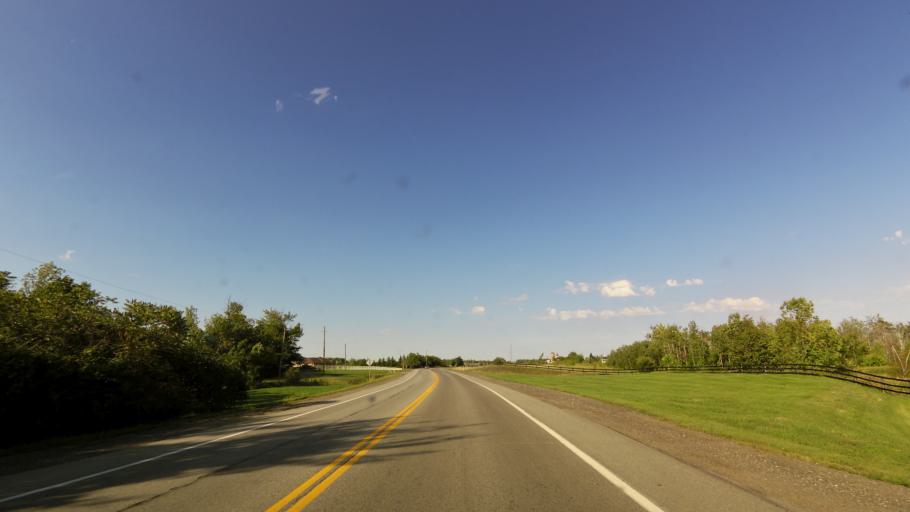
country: CA
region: Ontario
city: Brampton
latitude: 43.7393
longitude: -79.9153
